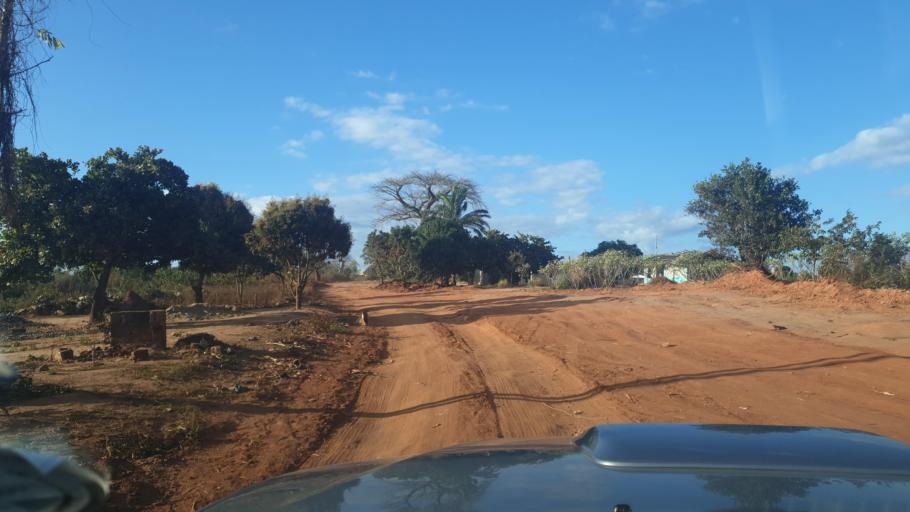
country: MZ
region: Nampula
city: Nampula
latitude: -15.1544
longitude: 39.2654
